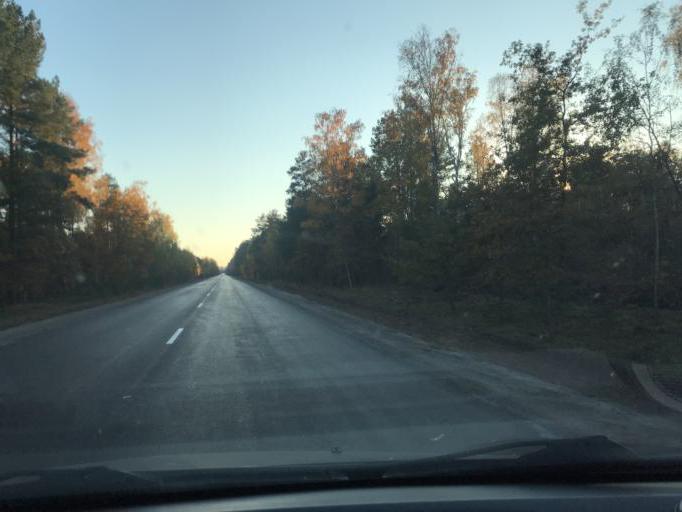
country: BY
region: Gomel
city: Brahin
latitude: 51.8731
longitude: 30.3822
